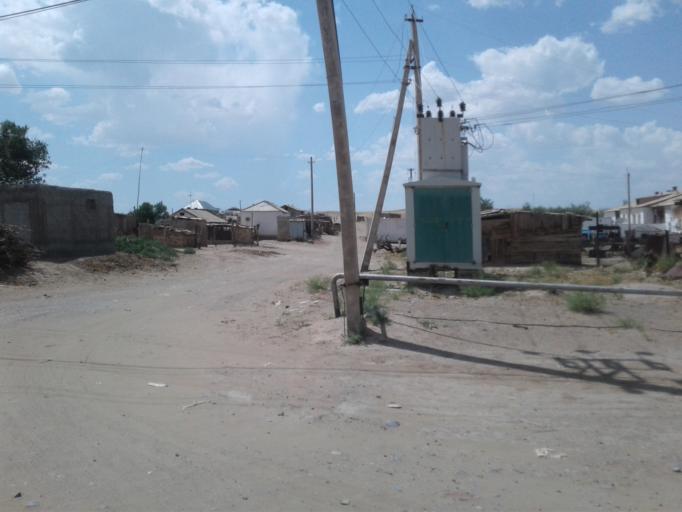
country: TM
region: Ahal
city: Abadan
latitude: 38.7642
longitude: 58.4926
